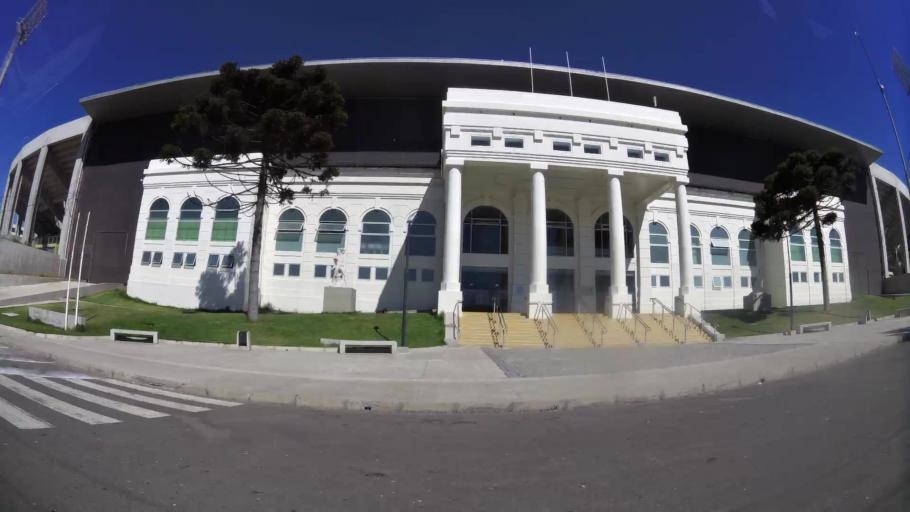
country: CL
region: Valparaiso
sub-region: Provincia de Valparaiso
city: Valparaiso
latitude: -33.0218
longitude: -71.6407
